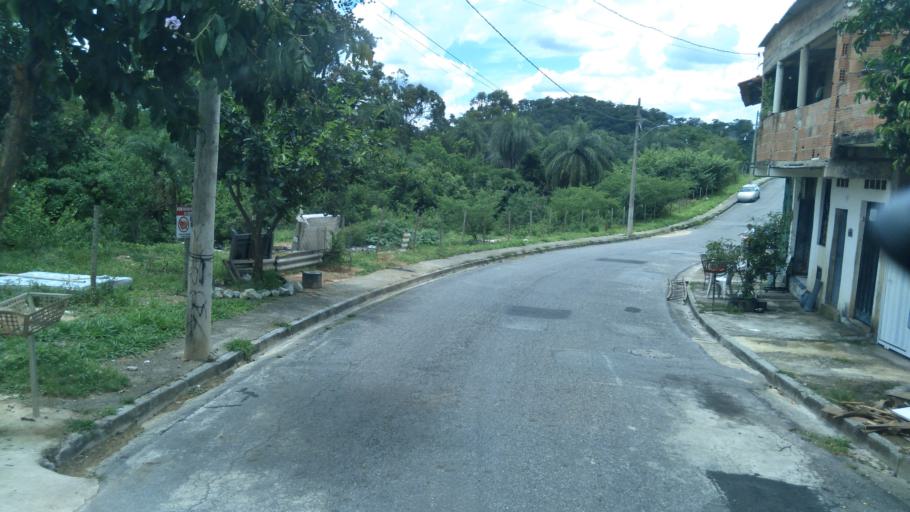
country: BR
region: Minas Gerais
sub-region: Belo Horizonte
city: Belo Horizonte
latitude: -19.8573
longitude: -43.8758
